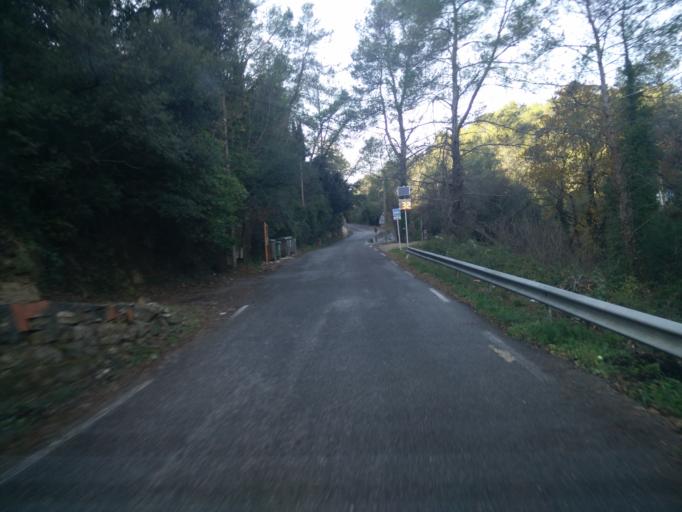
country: FR
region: Provence-Alpes-Cote d'Azur
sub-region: Departement du Var
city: Sollies-Toucas
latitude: 43.2033
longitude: 6.0162
